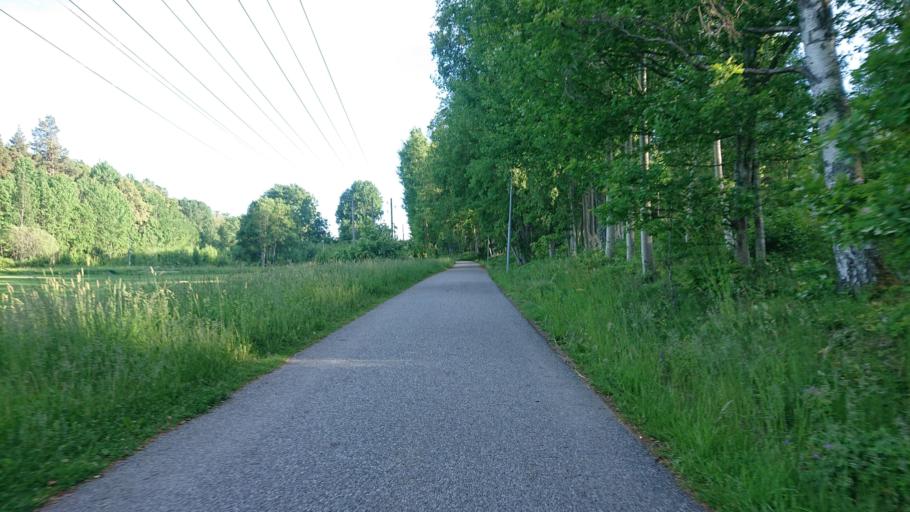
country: SE
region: Stockholm
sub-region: Osterakers Kommun
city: Akersberga
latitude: 59.4943
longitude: 18.3024
